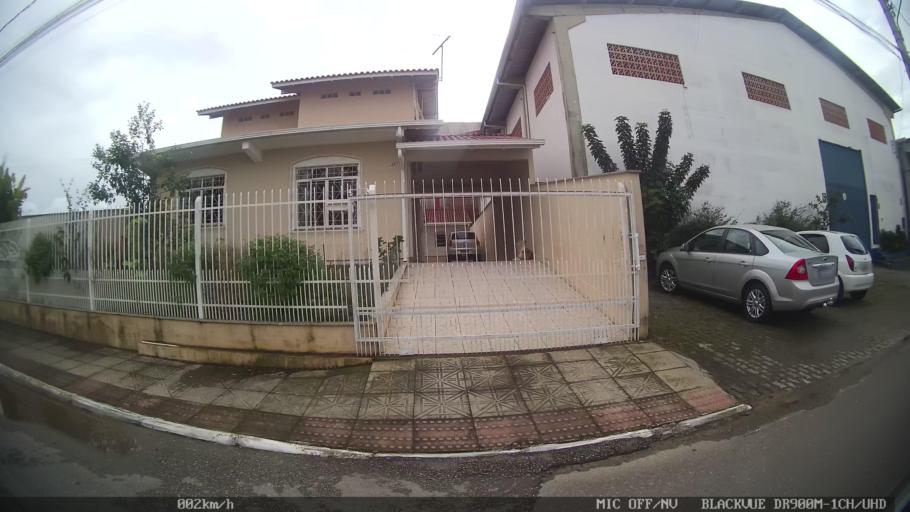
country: BR
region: Santa Catarina
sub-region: Sao Jose
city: Campinas
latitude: -27.5506
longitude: -48.6256
